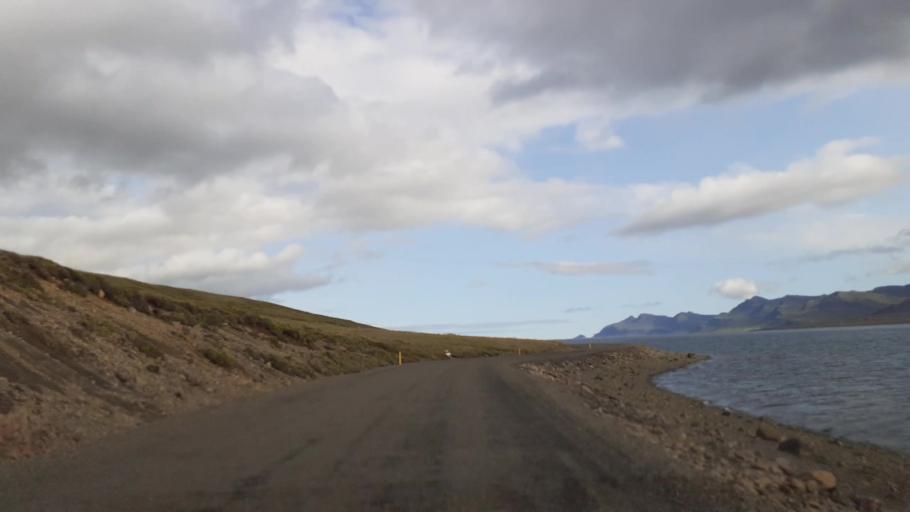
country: IS
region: East
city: Eskifjoerdur
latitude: 65.0579
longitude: -13.9847
